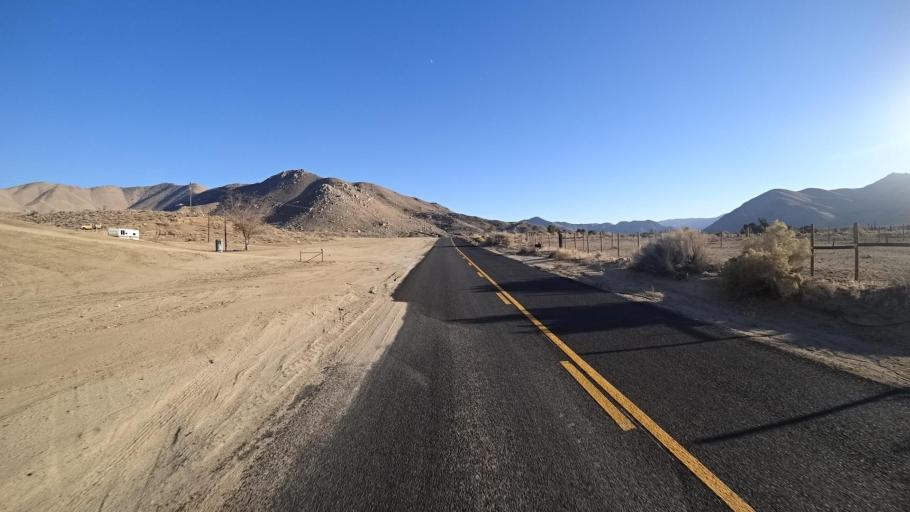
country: US
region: California
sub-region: Kern County
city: Weldon
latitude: 35.6377
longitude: -118.2470
